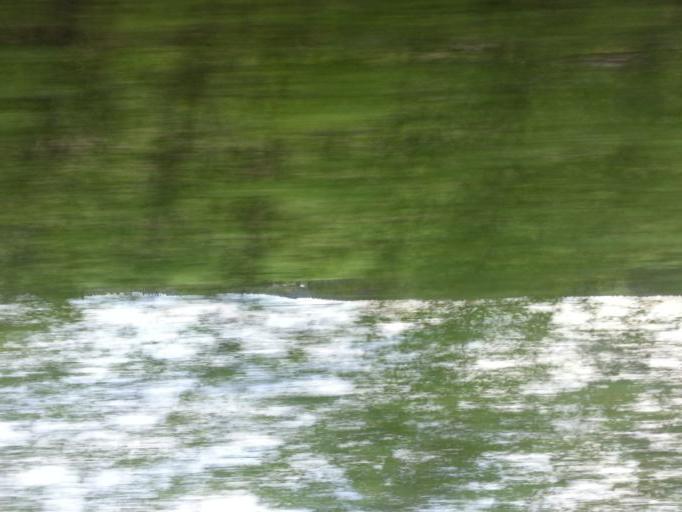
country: NO
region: Akershus
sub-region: Eidsvoll
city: Eidsvoll
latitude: 60.3124
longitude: 11.2307
